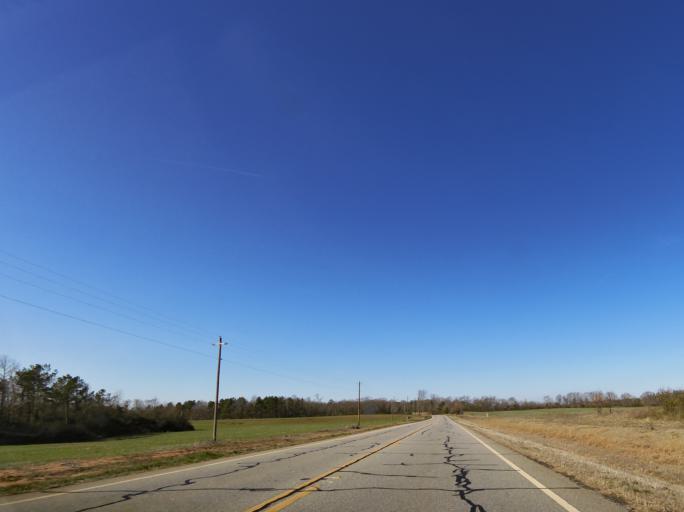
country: US
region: Georgia
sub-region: Lamar County
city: Barnesville
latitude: 32.8935
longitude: -84.1074
